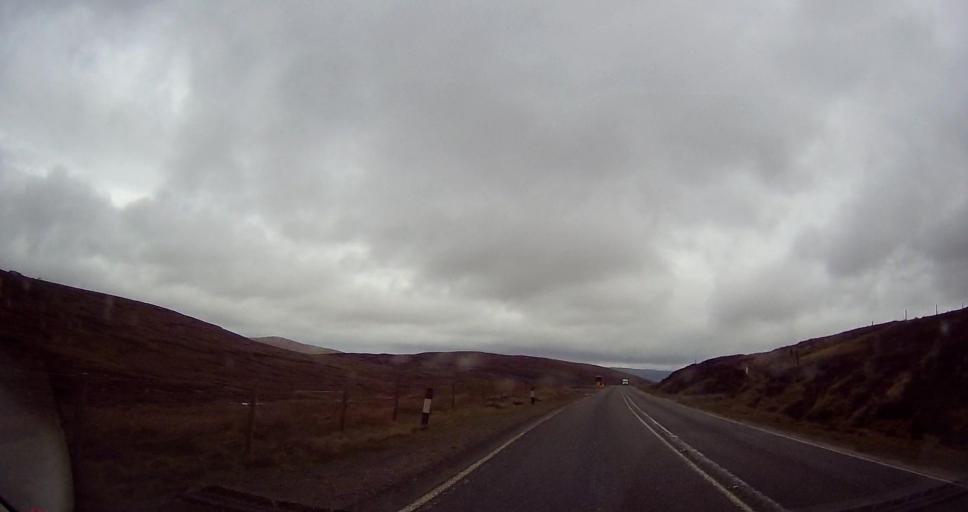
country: GB
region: Scotland
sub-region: Shetland Islands
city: Lerwick
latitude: 60.3222
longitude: -1.2516
